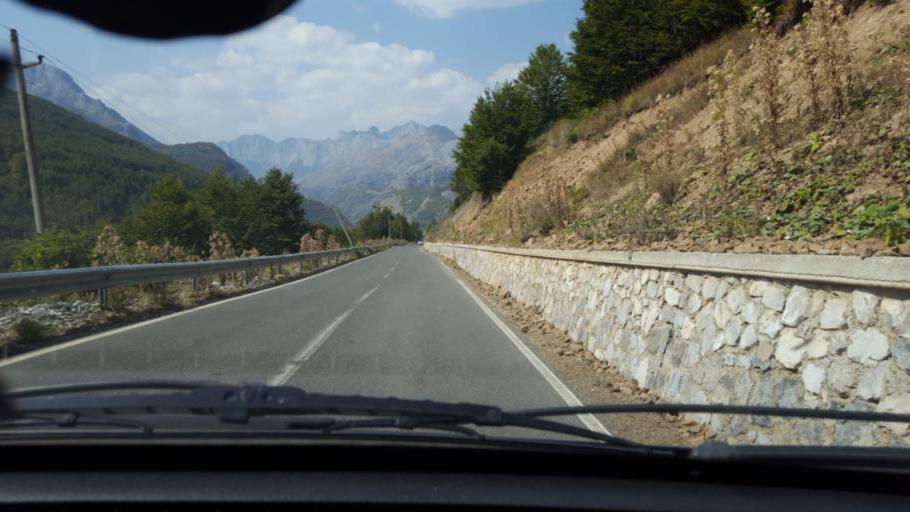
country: AL
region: Kukes
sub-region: Rrethi i Tropojes
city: Valbone
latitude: 42.5345
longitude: 19.7116
